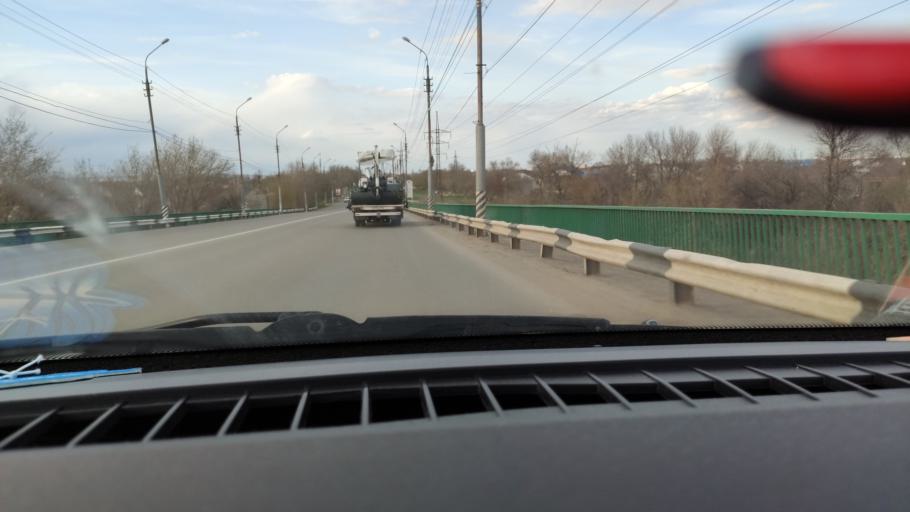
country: RU
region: Saratov
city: Privolzhskiy
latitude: 51.4202
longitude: 46.0470
